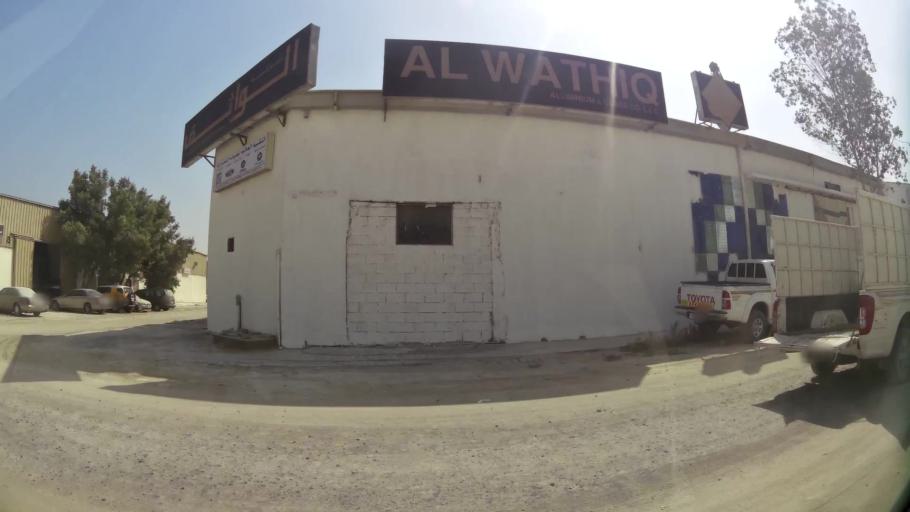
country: AE
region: Ash Shariqah
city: Sharjah
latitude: 25.3068
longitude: 55.3842
